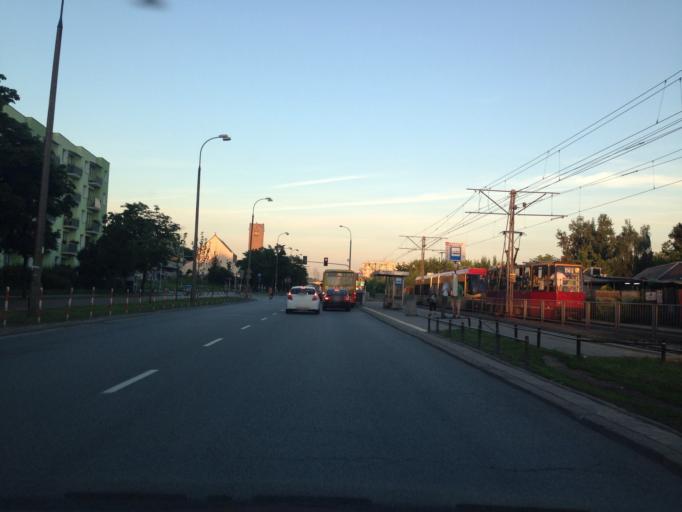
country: PL
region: Masovian Voivodeship
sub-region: Warszawa
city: Bielany
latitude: 52.2697
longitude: 20.9525
